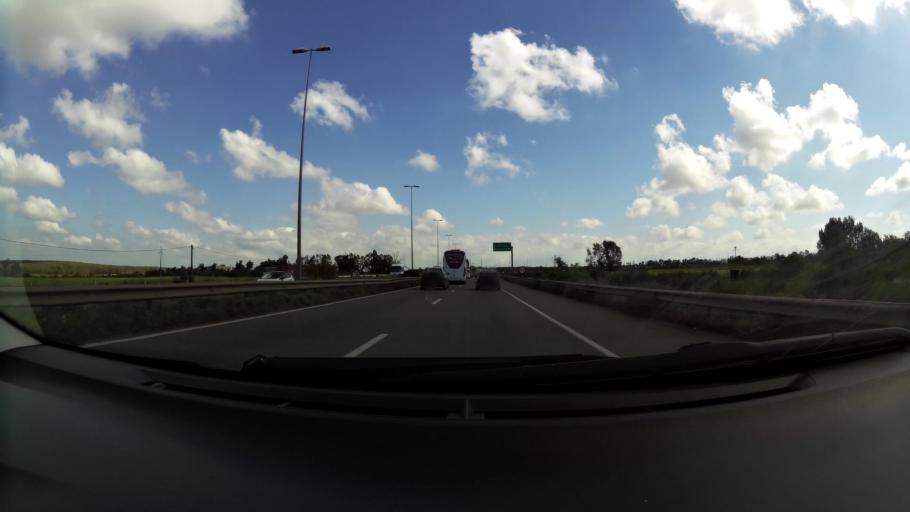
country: MA
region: Grand Casablanca
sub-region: Nouaceur
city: Bouskoura
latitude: 33.4420
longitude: -7.6310
